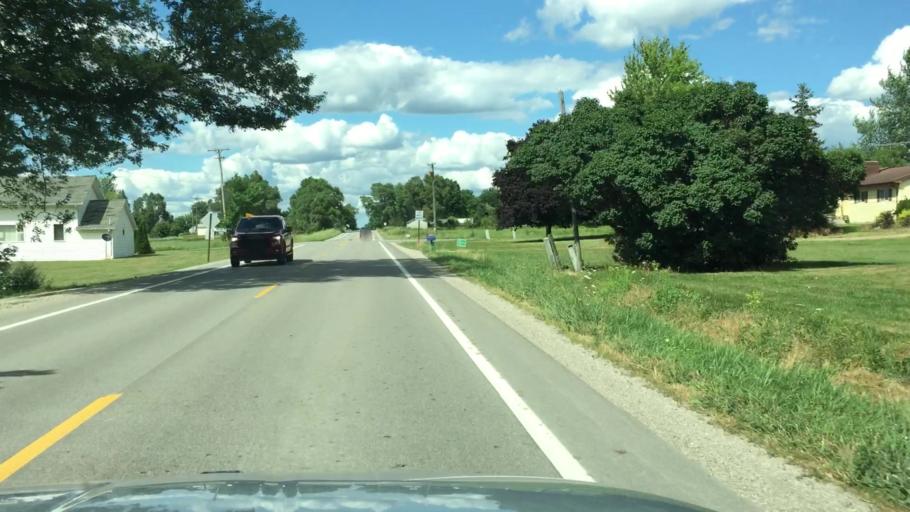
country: US
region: Michigan
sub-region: Saint Clair County
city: Capac
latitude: 42.9668
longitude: -82.9364
